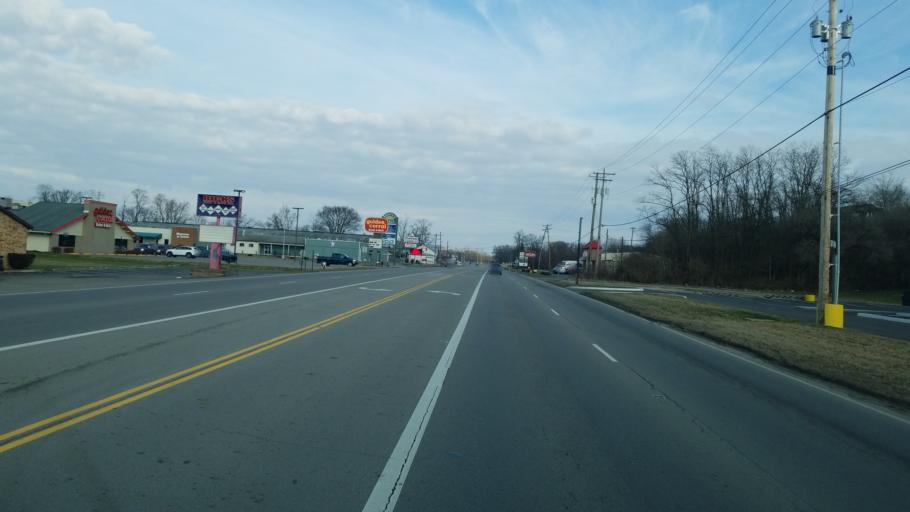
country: US
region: Ohio
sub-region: Ross County
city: Chillicothe
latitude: 39.3689
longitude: -82.9757
